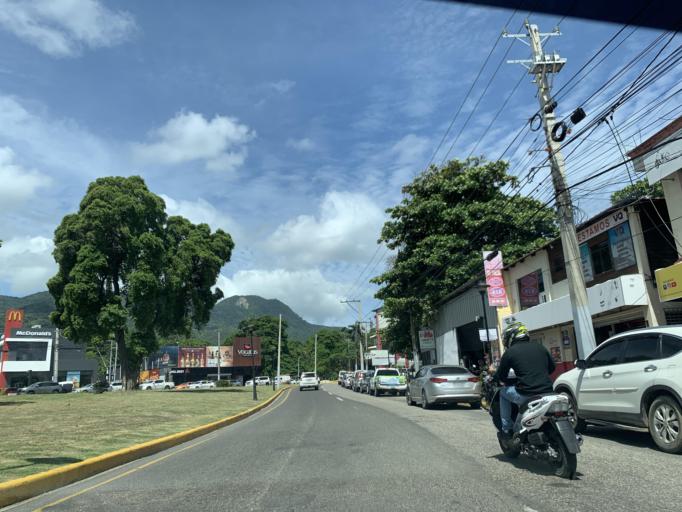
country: DO
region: Puerto Plata
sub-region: Puerto Plata
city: Puerto Plata
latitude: 19.7832
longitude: -70.6737
